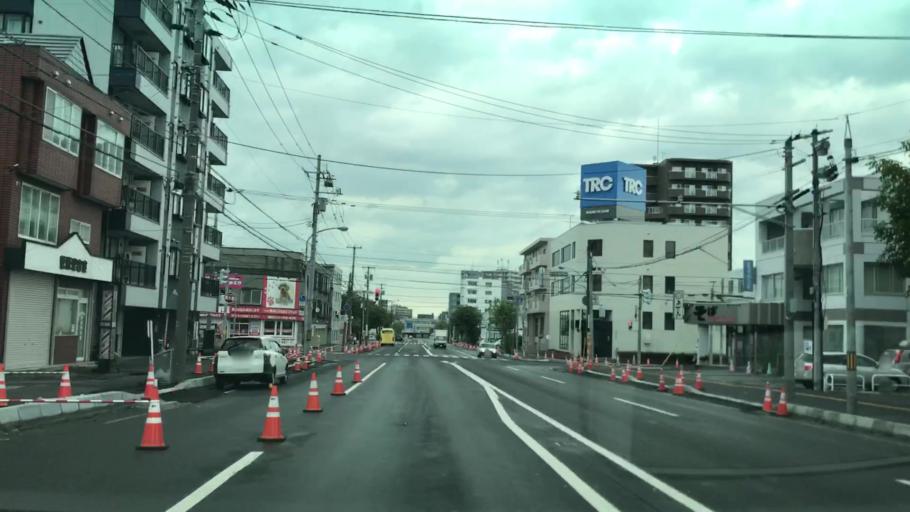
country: JP
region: Hokkaido
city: Sapporo
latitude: 43.0519
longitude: 141.3717
